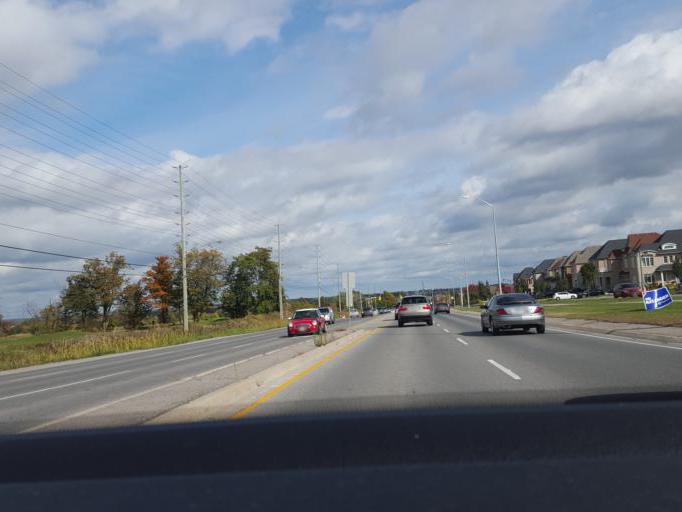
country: CA
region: Ontario
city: Ajax
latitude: 43.8987
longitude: -79.0277
